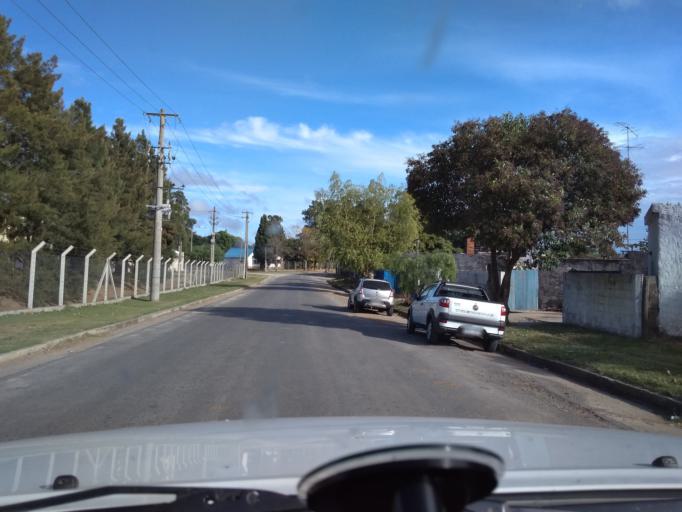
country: UY
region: Florida
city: Florida
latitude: -34.1074
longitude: -56.2156
